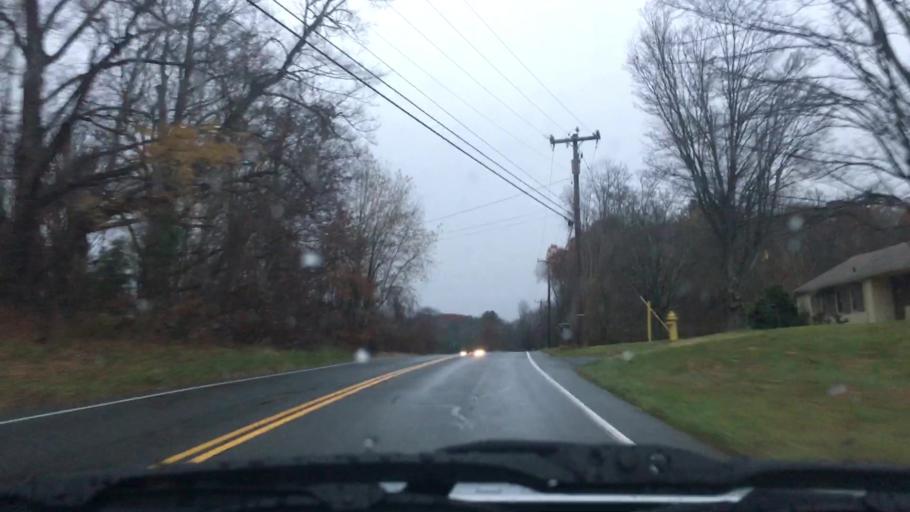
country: US
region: Massachusetts
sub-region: Hampden County
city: Southwick
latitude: 42.0636
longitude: -72.7176
